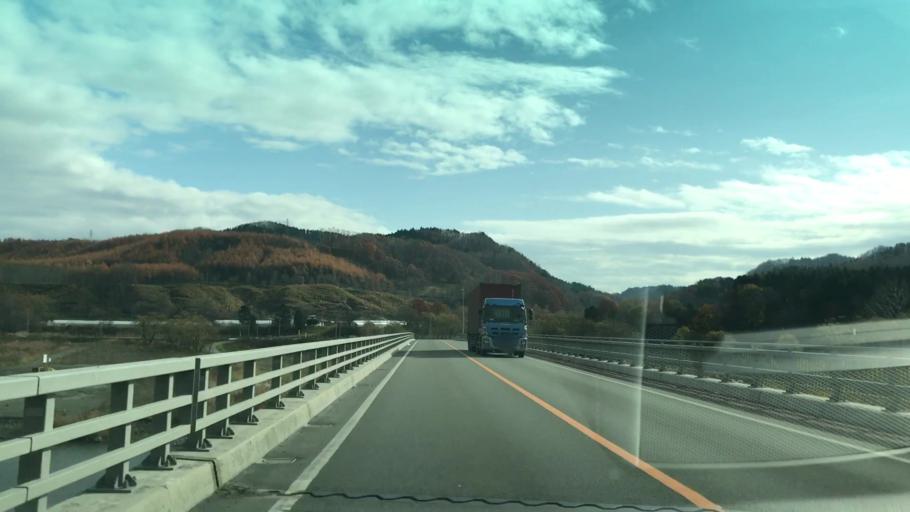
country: JP
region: Hokkaido
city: Shizunai-furukawacho
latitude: 42.7263
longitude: 142.3121
